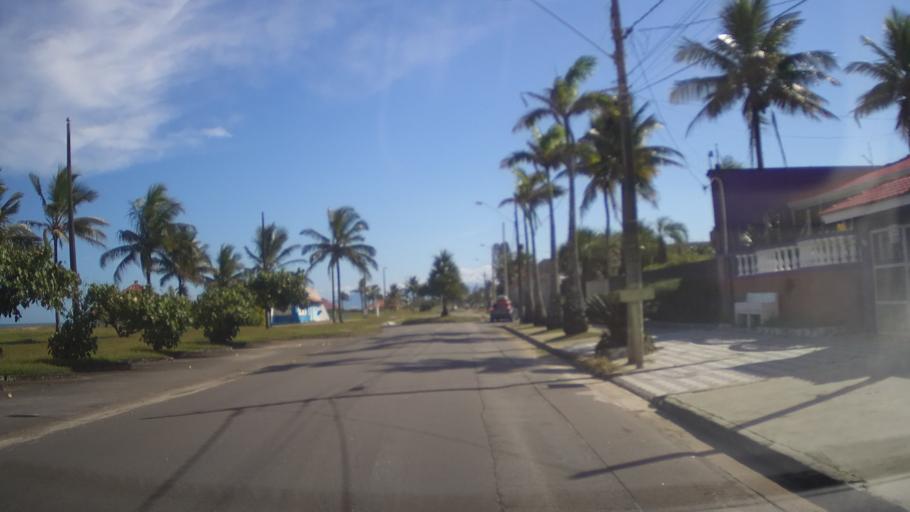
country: BR
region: Sao Paulo
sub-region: Itanhaem
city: Itanhaem
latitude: -24.2057
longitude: -46.8264
